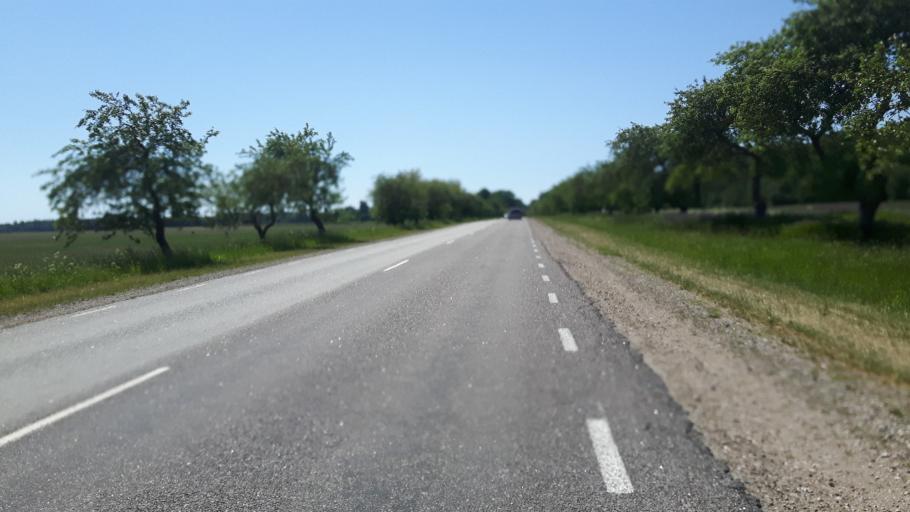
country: EE
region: Paernumaa
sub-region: Tootsi vald
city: Tootsi
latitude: 58.4728
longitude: 24.7986
